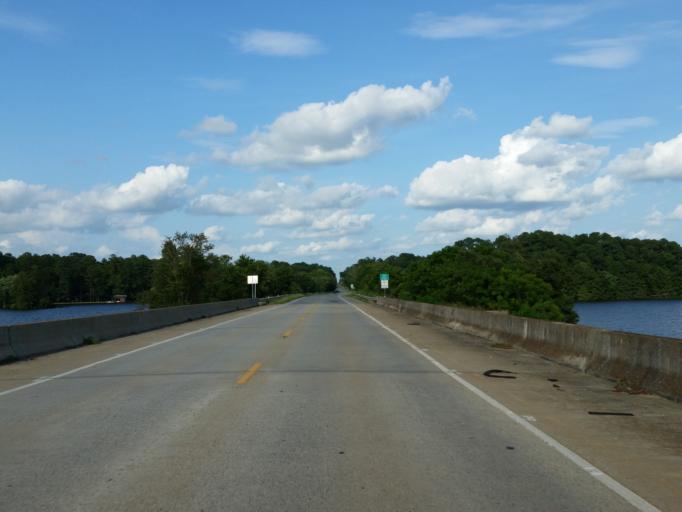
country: US
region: Georgia
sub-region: Crisp County
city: Cordele
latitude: 31.9654
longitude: -83.9294
